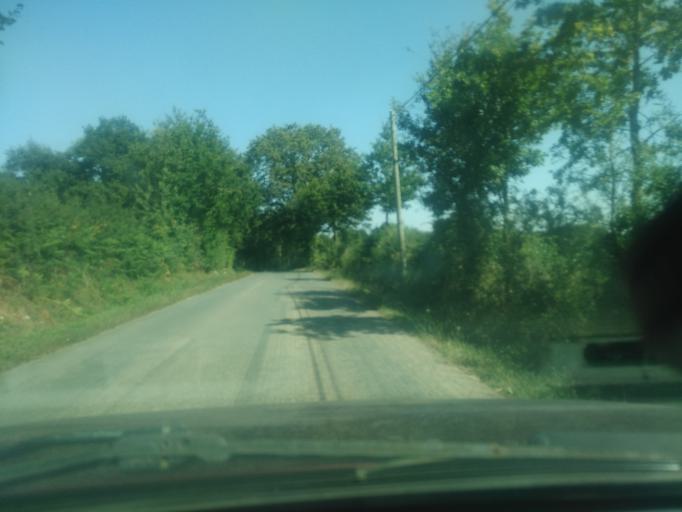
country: FR
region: Pays de la Loire
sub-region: Departement de la Vendee
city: La Ferriere
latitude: 46.7159
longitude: -1.3487
